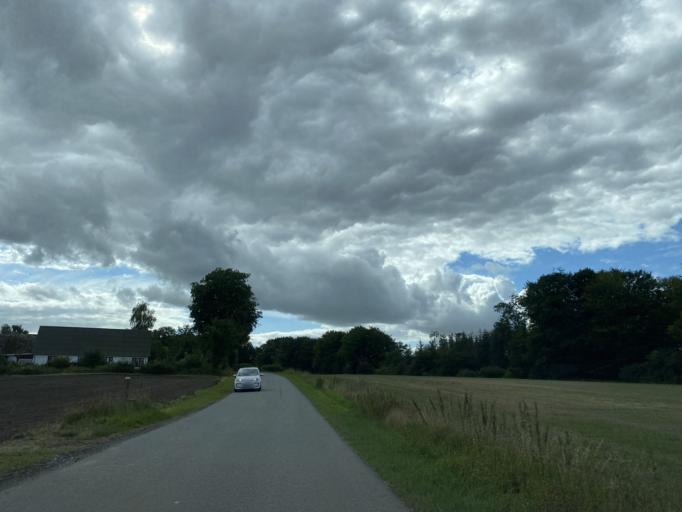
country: DK
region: Central Jutland
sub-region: Horsens Kommune
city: Horsens
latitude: 55.9581
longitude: 9.8575
